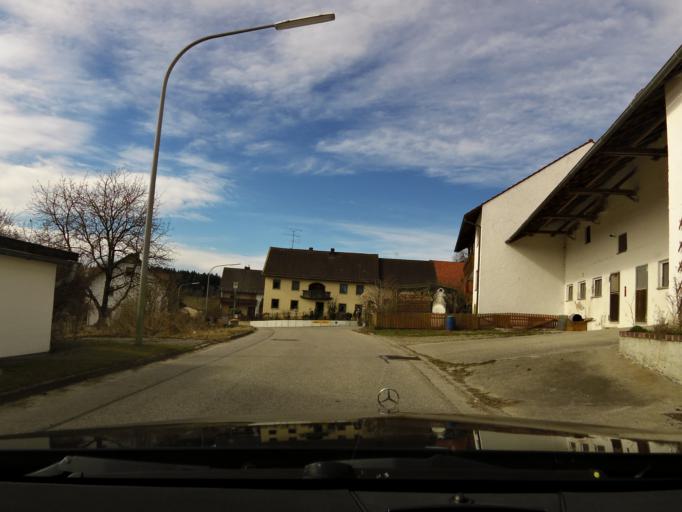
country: DE
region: Bavaria
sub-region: Lower Bavaria
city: Furth
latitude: 48.5564
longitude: 12.0396
